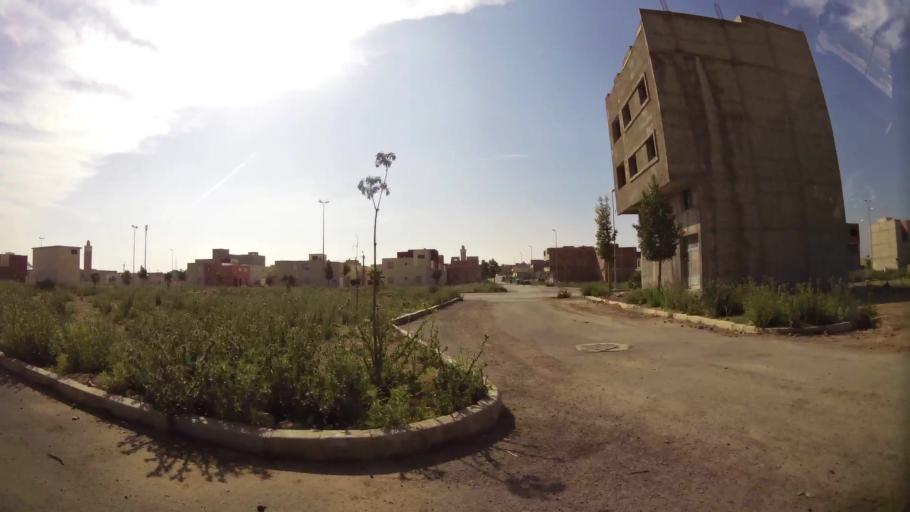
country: MA
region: Oriental
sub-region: Oujda-Angad
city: Oujda
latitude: 34.7103
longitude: -1.8786
